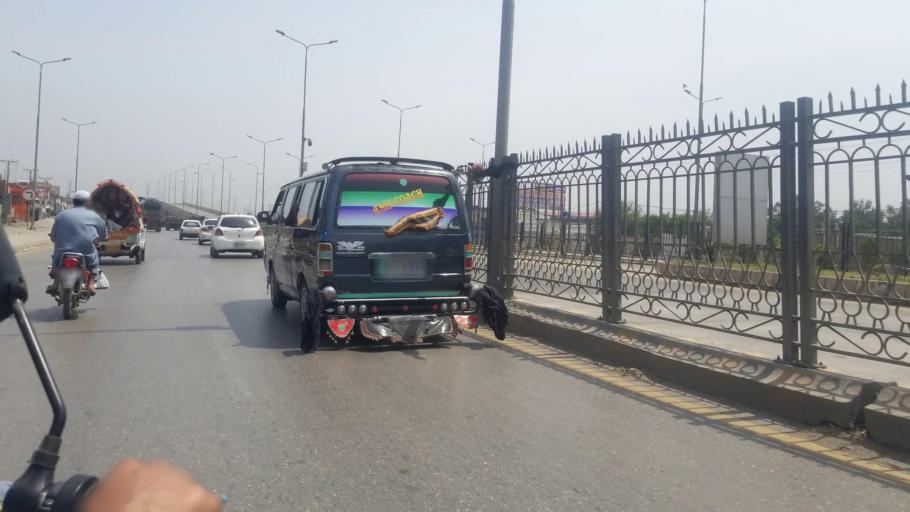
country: PK
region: Khyber Pakhtunkhwa
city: Peshawar
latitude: 34.0192
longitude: 71.6403
